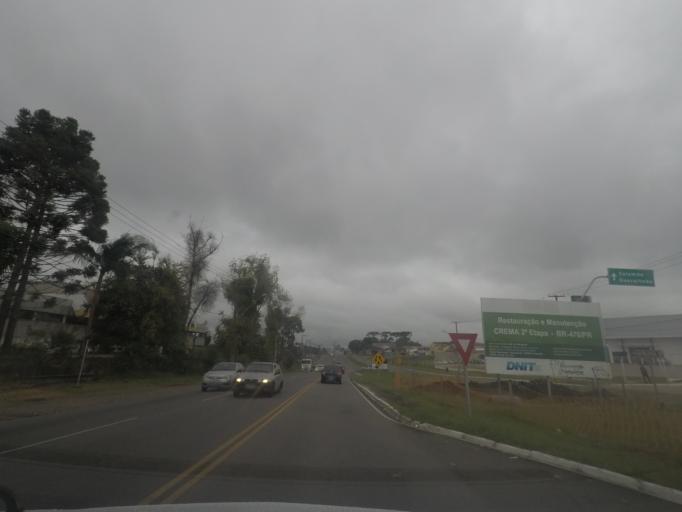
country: BR
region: Parana
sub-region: Pinhais
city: Pinhais
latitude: -25.3873
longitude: -49.2047
